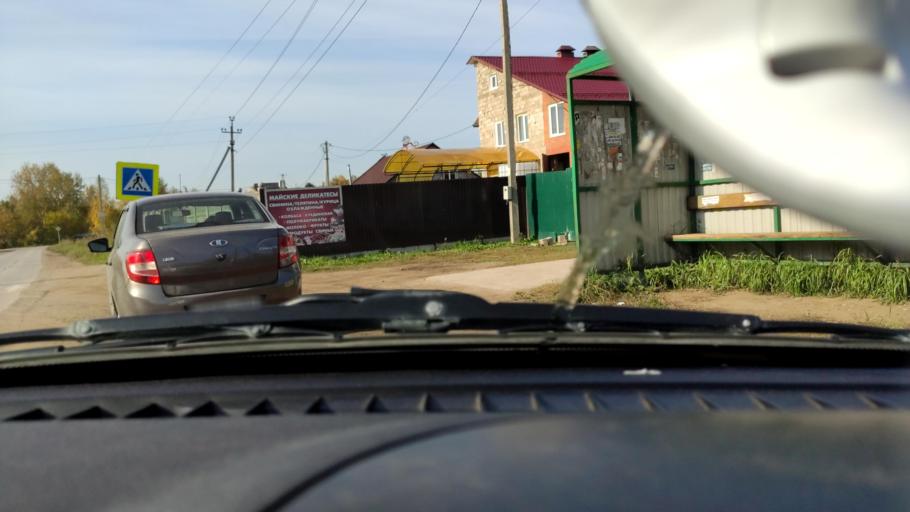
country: RU
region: Perm
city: Overyata
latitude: 58.0895
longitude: 55.8695
